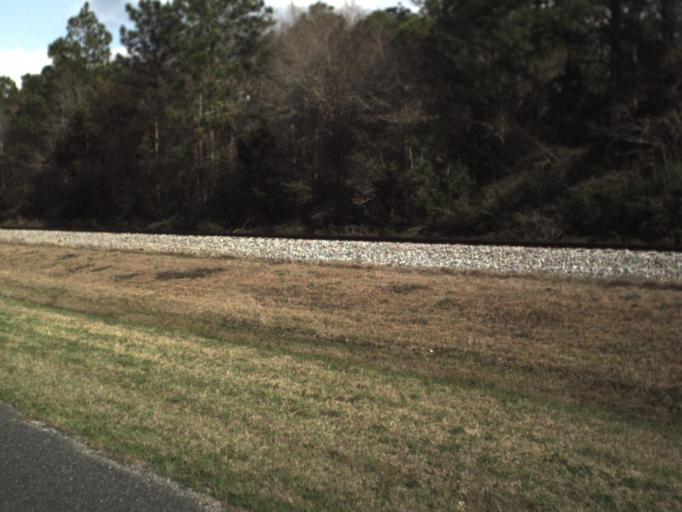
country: US
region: Florida
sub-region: Bay County
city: Youngstown
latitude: 30.3072
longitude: -85.4744
